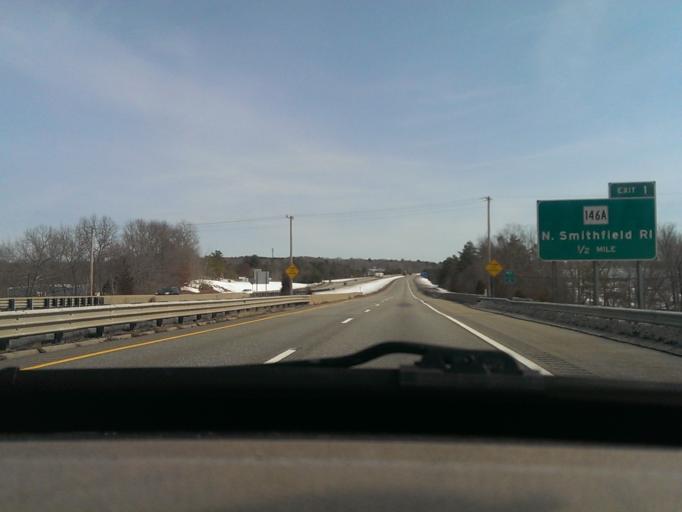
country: US
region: Massachusetts
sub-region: Worcester County
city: Millville
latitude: 42.0277
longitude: -71.6121
